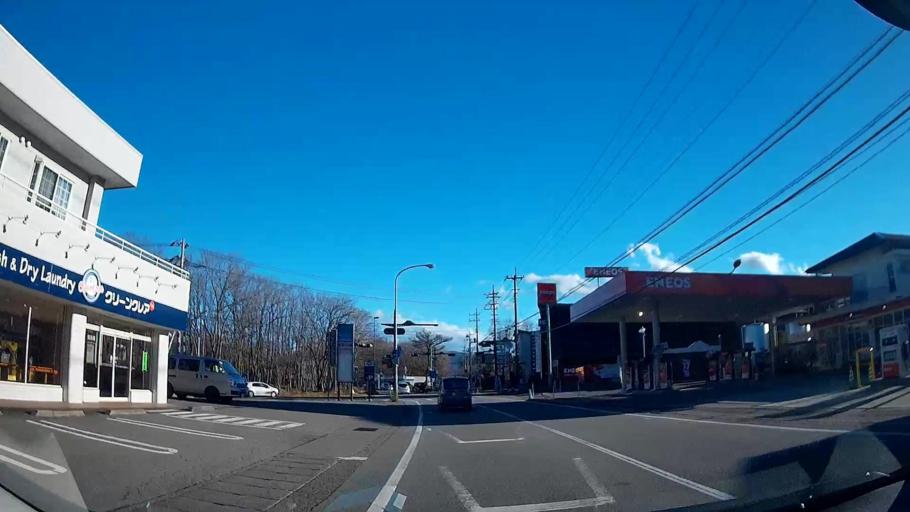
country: JP
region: Shizuoka
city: Gotemba
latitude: 35.4297
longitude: 138.8451
